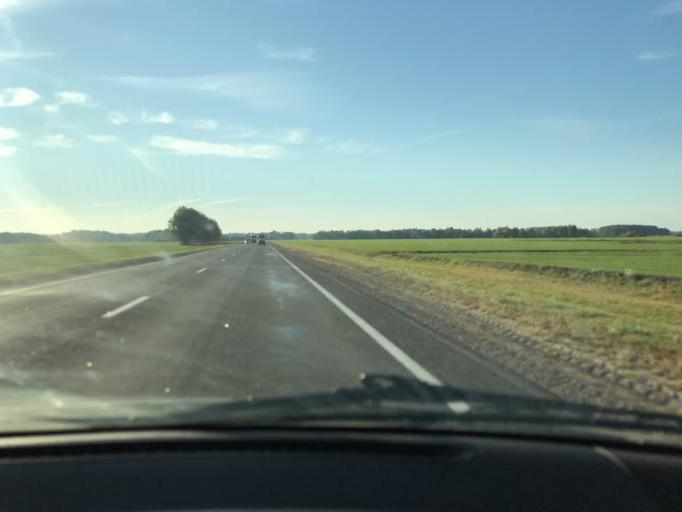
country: BY
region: Brest
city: Antopal'
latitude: 52.2072
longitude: 24.5873
